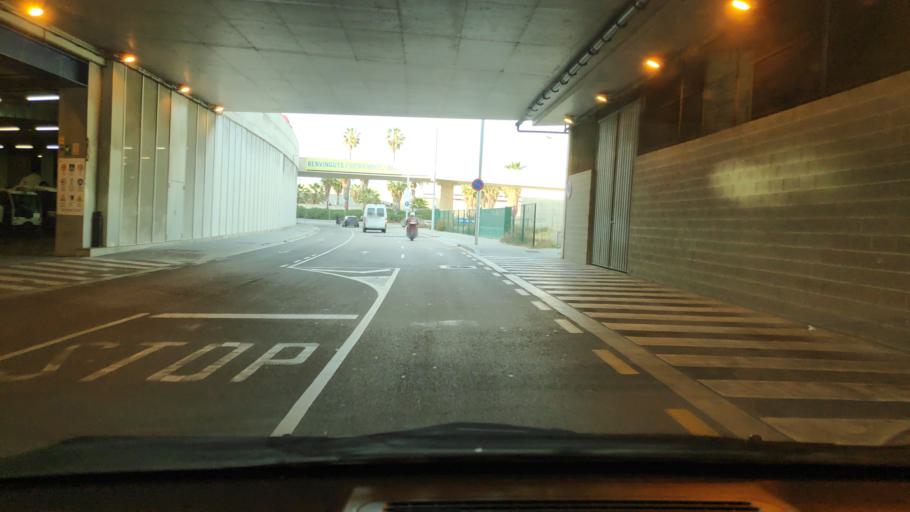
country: ES
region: Catalonia
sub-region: Provincia de Barcelona
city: Sant Adria de Besos
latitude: 41.4086
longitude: 2.2221
